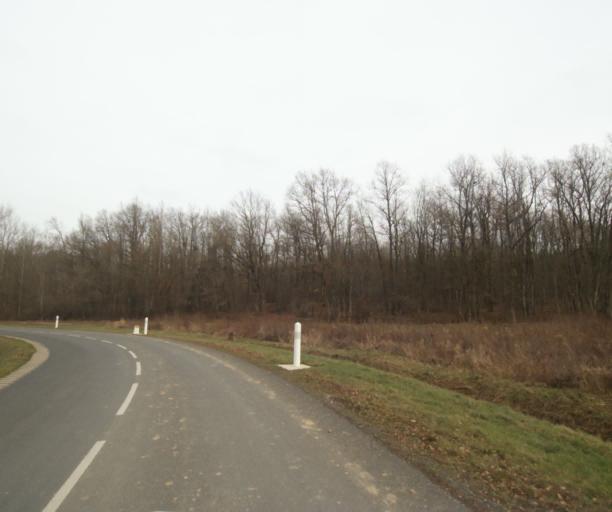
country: FR
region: Champagne-Ardenne
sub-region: Departement de la Marne
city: Pargny-sur-Saulx
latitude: 48.7460
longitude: 4.8618
